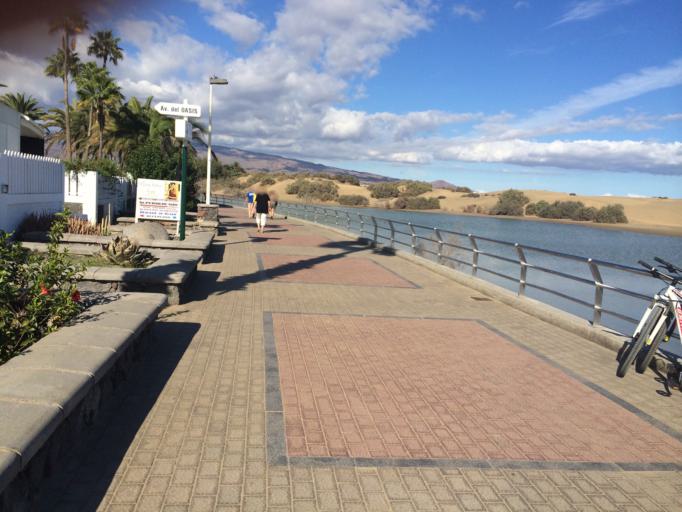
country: ES
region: Canary Islands
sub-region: Provincia de Las Palmas
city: Maspalomas
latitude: 27.7370
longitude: -15.5945
